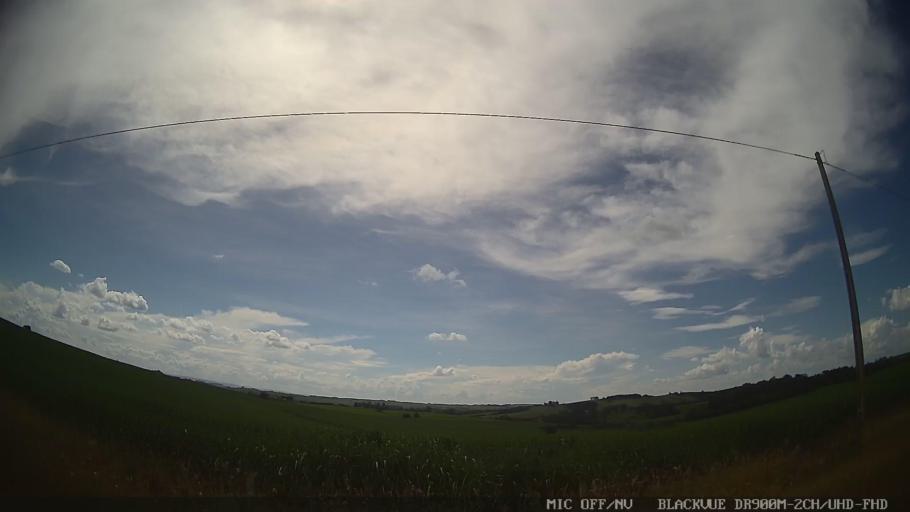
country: BR
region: Sao Paulo
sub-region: Conchas
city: Conchas
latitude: -22.9731
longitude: -47.9864
